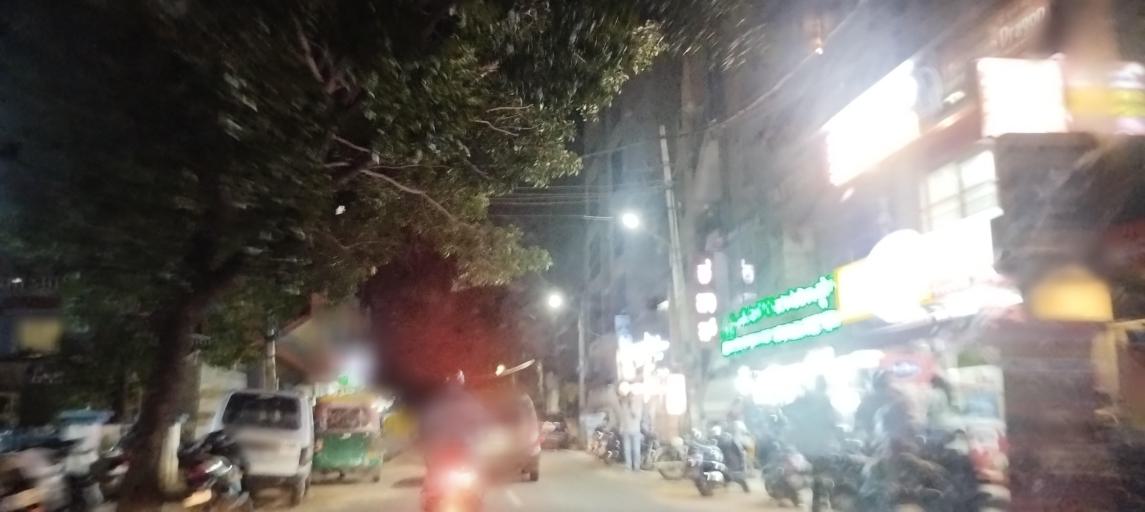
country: IN
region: Karnataka
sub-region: Bangalore Urban
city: Bangalore
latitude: 12.9400
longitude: 77.5643
